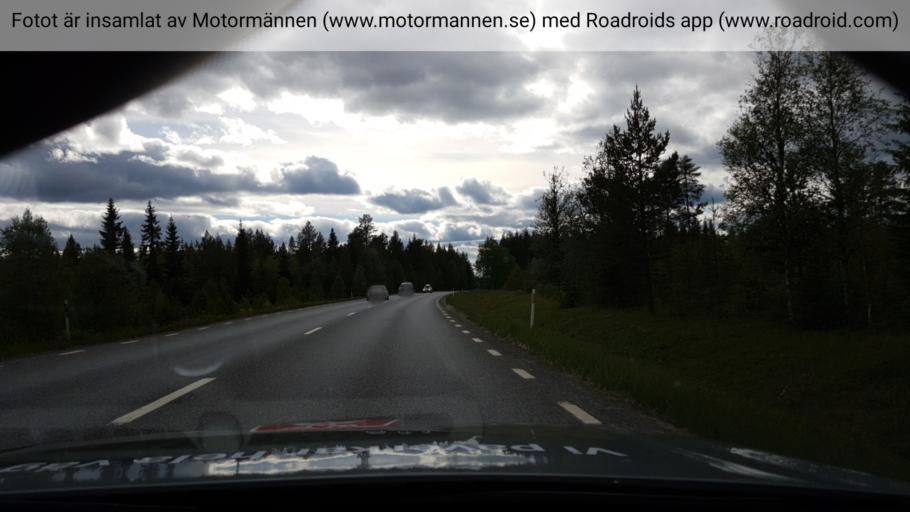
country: SE
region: Jaemtland
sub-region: OEstersunds Kommun
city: Lit
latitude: 63.3937
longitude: 15.0224
